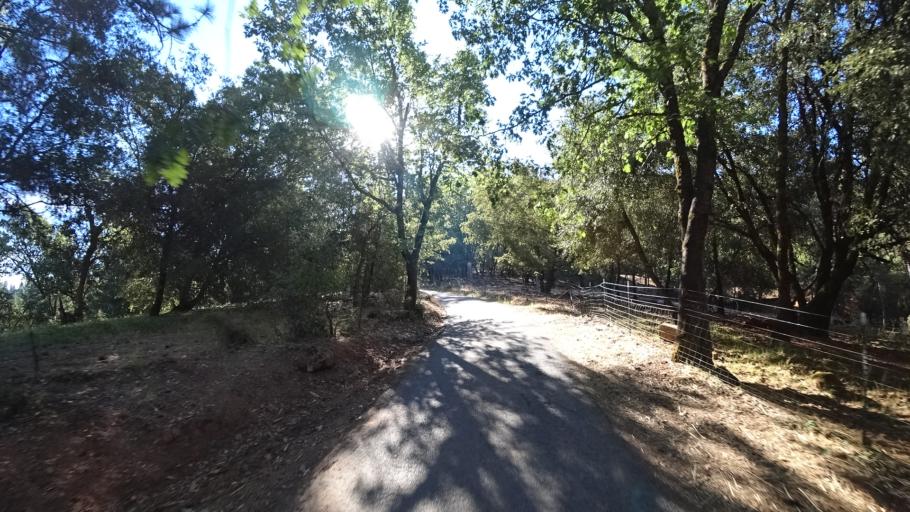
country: US
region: California
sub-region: Amador County
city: Pioneer
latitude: 38.3847
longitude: -120.5625
